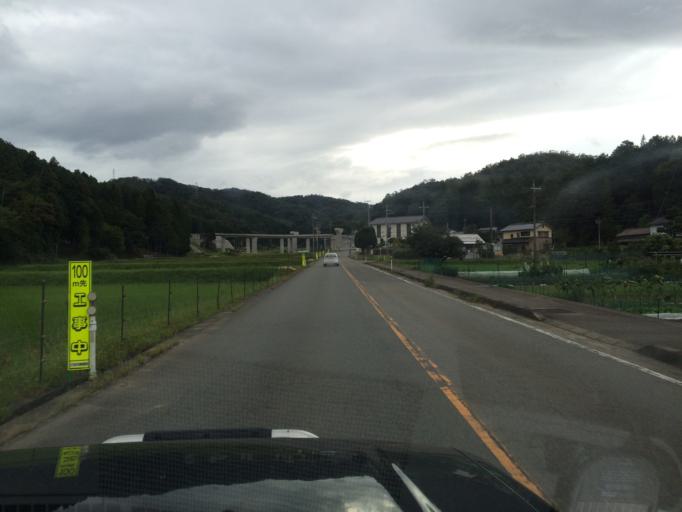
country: JP
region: Hyogo
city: Toyooka
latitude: 35.5081
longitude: 134.8080
